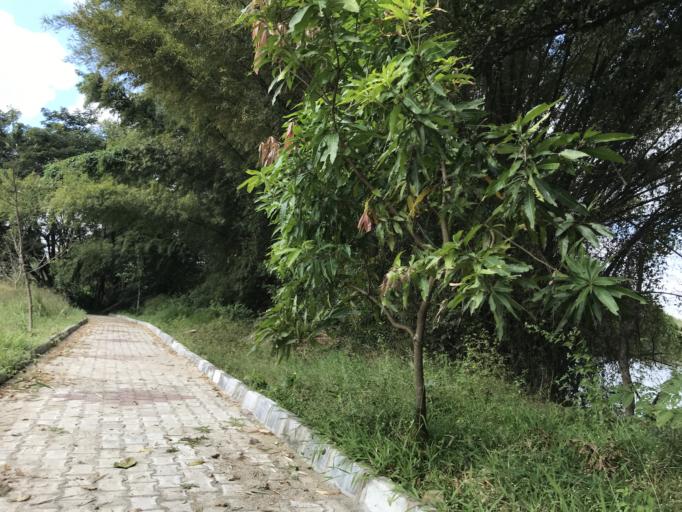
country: IN
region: Karnataka
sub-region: Mandya
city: Shrirangapattana
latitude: 12.4241
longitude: 76.6513
